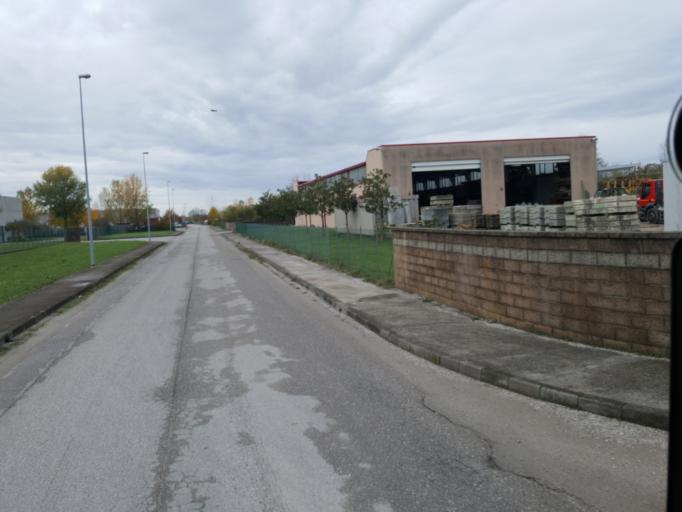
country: IT
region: Friuli Venezia Giulia
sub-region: Provincia di Udine
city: Manzano
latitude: 45.9873
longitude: 13.3621
